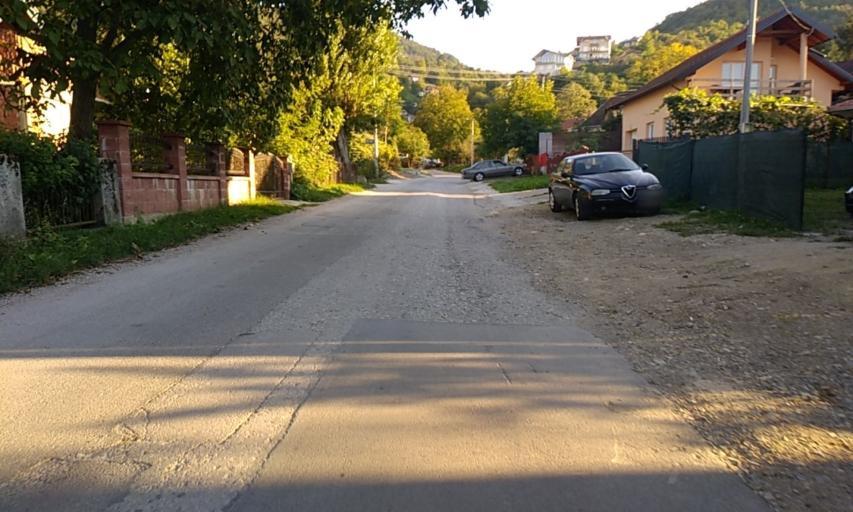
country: BA
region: Republika Srpska
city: Mejdan - Obilicevo
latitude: 44.7568
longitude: 17.1910
